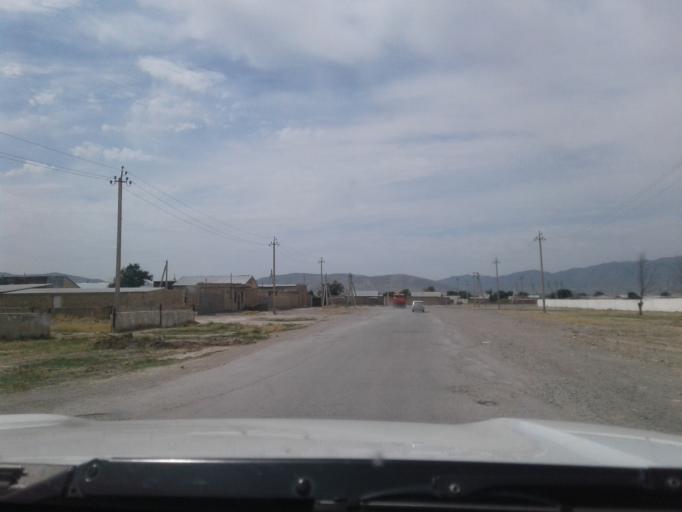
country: TM
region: Balkan
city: Serdar
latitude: 38.9934
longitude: 56.2701
